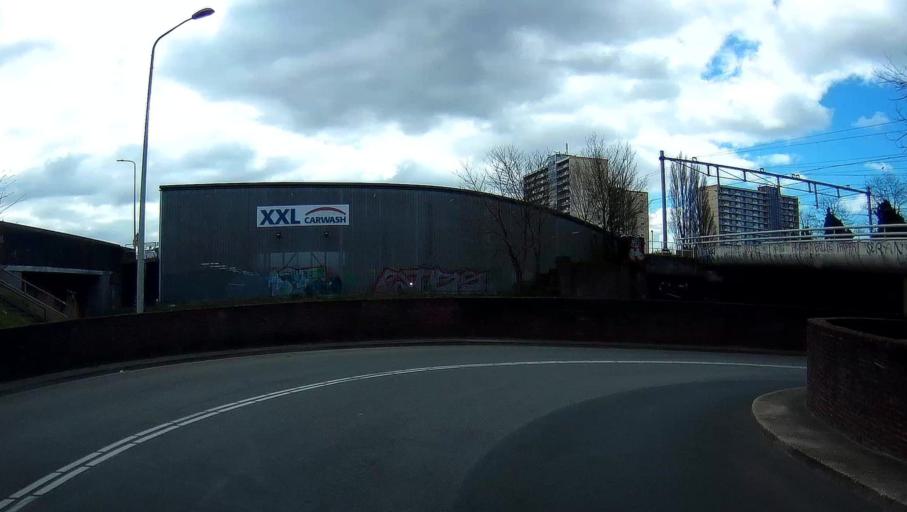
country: NL
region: South Holland
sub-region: Gemeente Den Haag
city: The Hague
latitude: 52.0585
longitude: 4.3099
